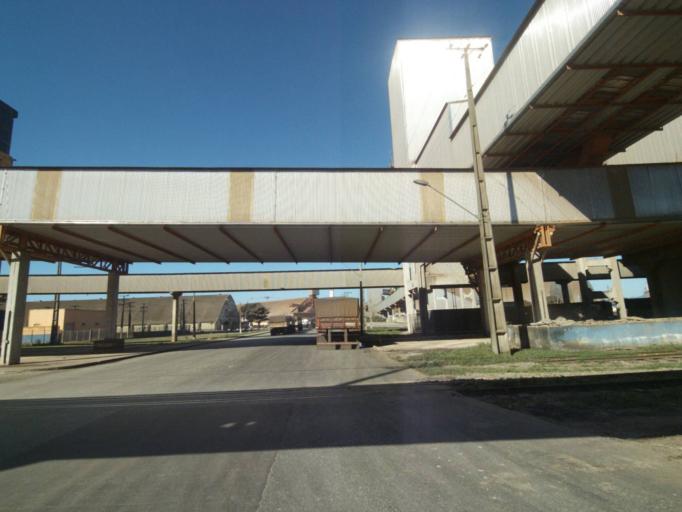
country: BR
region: Parana
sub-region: Paranagua
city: Paranagua
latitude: -25.5049
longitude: -48.5095
